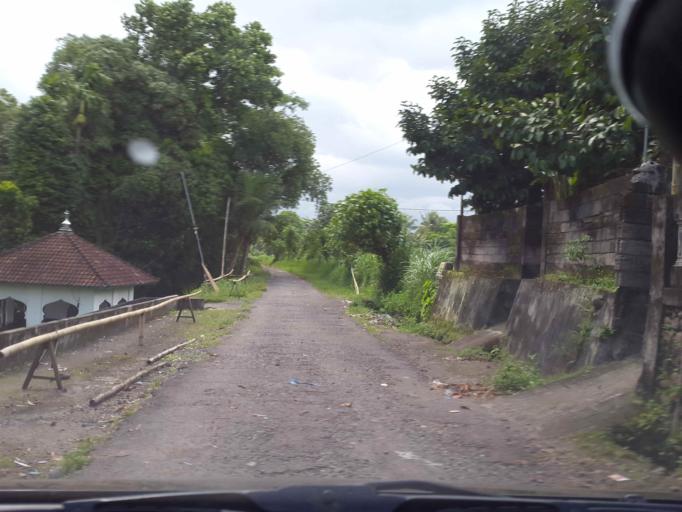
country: ID
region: West Nusa Tenggara
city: Batukuta
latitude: -8.6040
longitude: 116.1965
